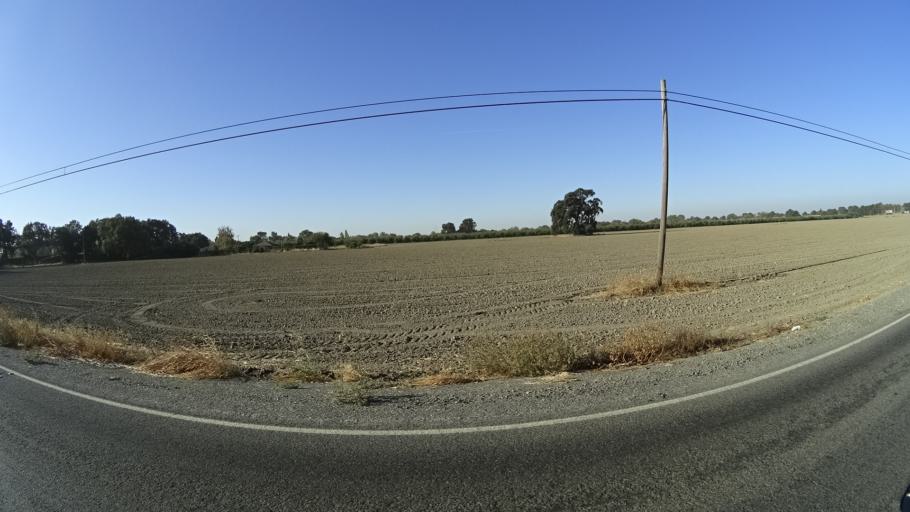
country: US
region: California
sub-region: Sacramento County
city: Walnut Grove
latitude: 38.3358
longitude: -121.5715
